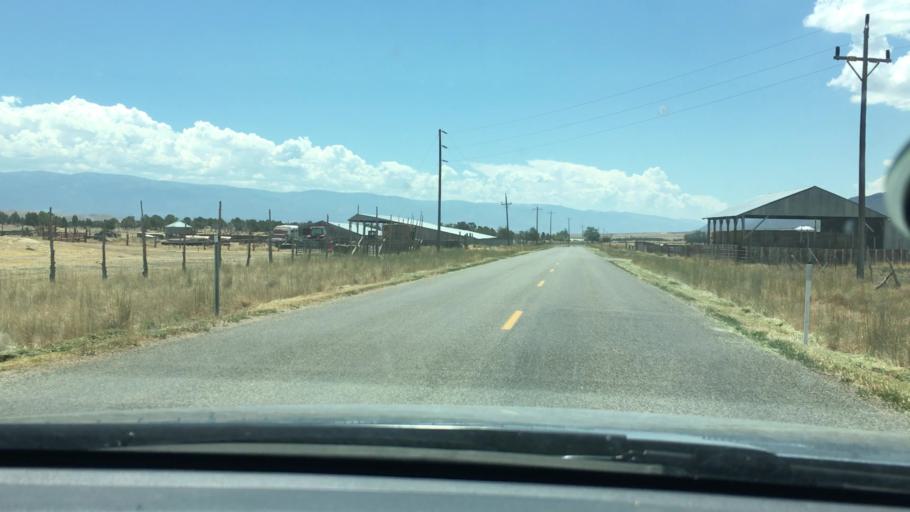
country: US
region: Utah
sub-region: Sanpete County
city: Fountain Green
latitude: 39.6104
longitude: -111.6446
